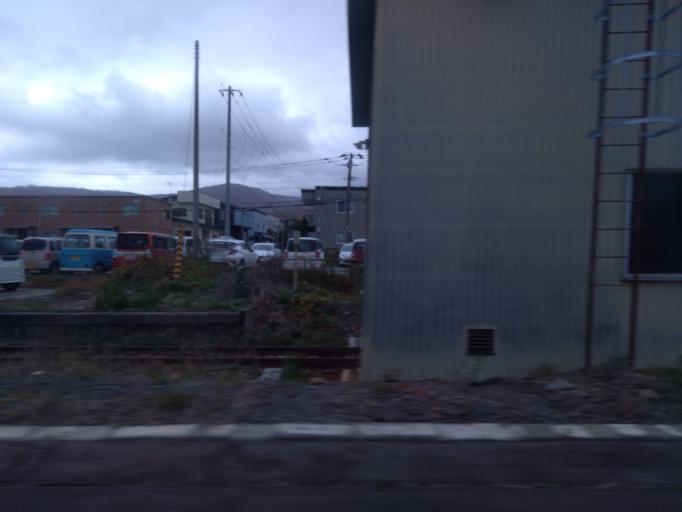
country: JP
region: Hokkaido
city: Nanae
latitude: 41.8872
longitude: 140.6886
